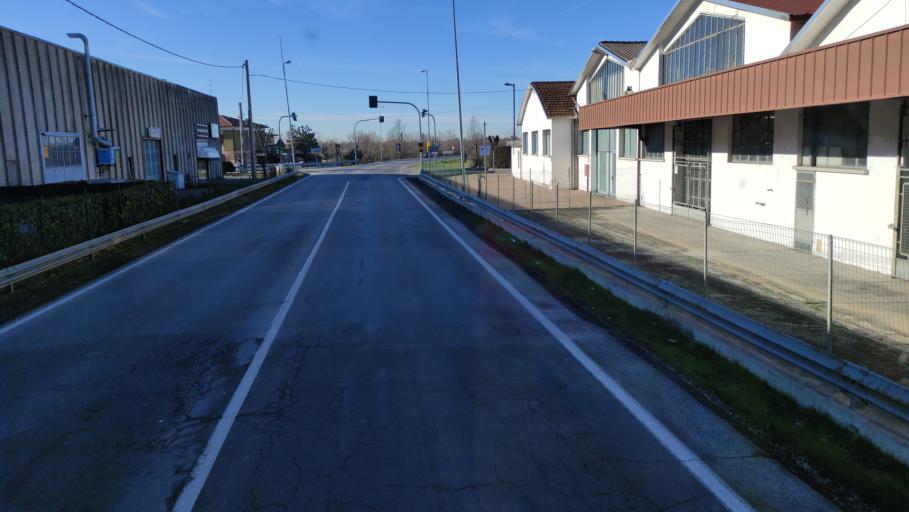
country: IT
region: Emilia-Romagna
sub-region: Provincia di Reggio Emilia
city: Campagnola Emilia
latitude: 44.8383
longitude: 10.7530
